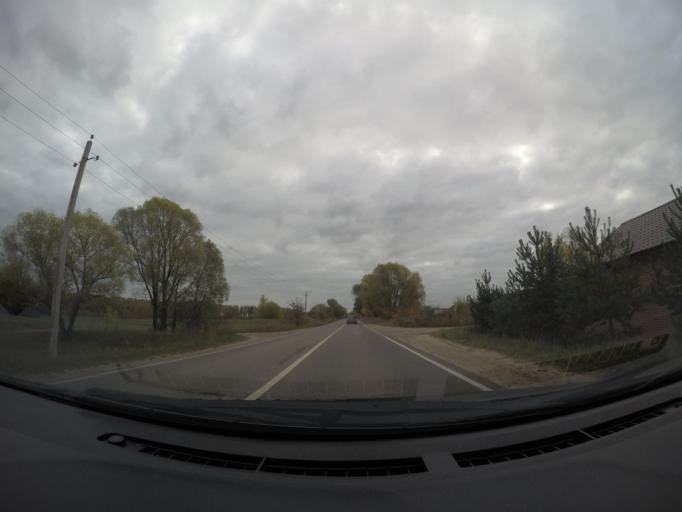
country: RU
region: Moskovskaya
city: Gzhel'
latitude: 55.6298
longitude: 38.4285
